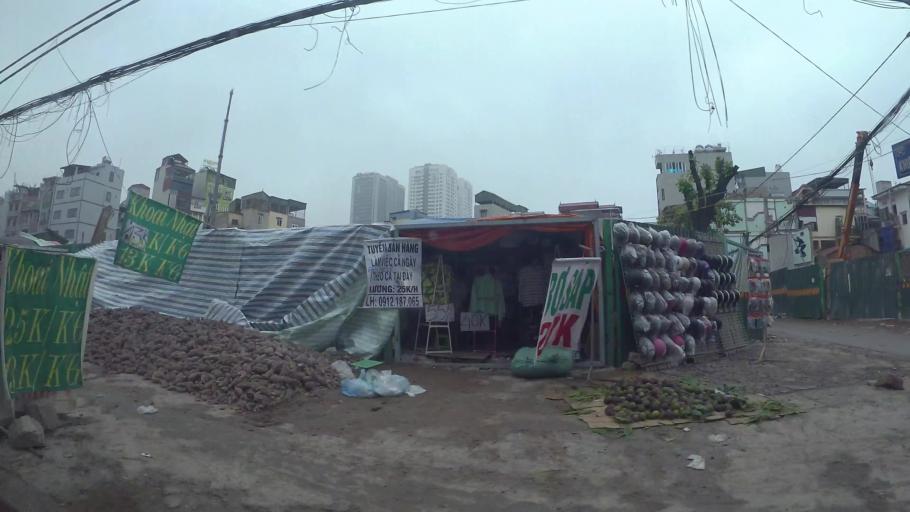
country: VN
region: Ha Noi
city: Dong Da
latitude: 21.0021
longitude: 105.8238
